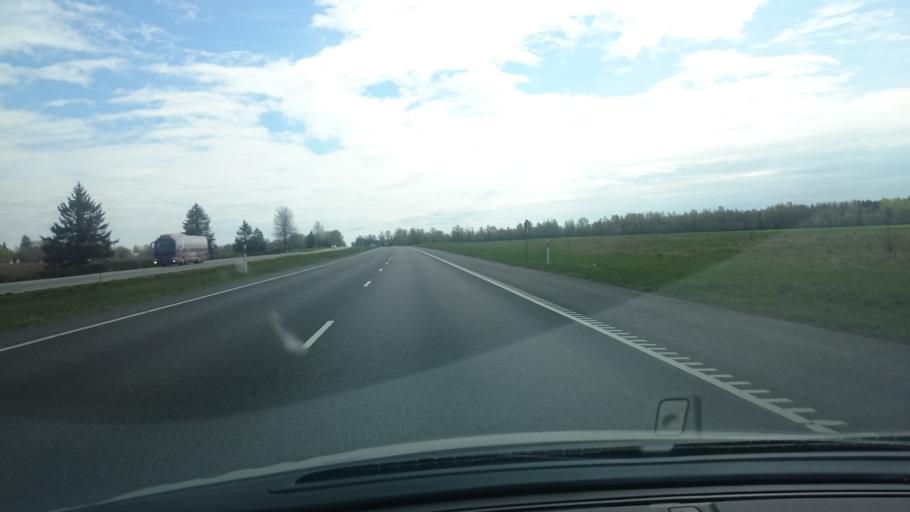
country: EE
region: Laeaene-Virumaa
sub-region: Kadrina vald
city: Kadrina
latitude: 59.4413
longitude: 26.1138
